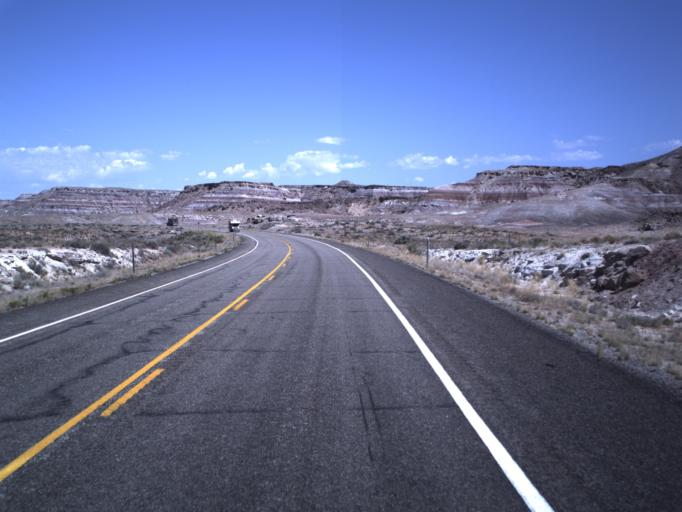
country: US
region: Utah
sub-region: Carbon County
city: East Carbon City
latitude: 38.8891
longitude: -110.3586
